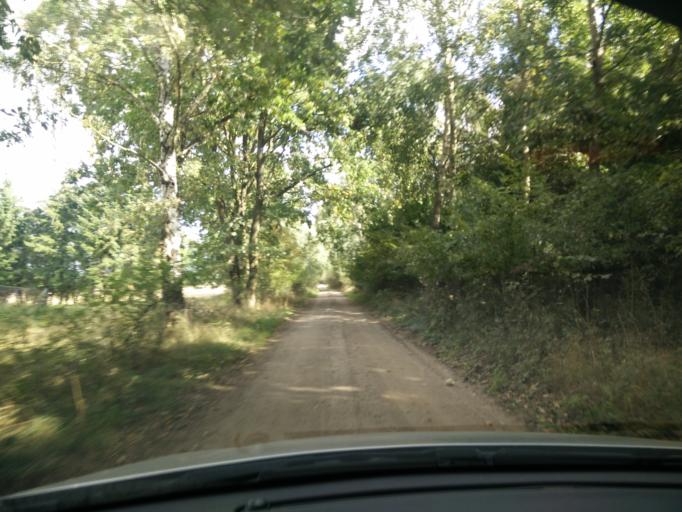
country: PL
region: Greater Poland Voivodeship
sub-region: Powiat sredzki
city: Sroda Wielkopolska
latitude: 52.2804
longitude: 17.2496
